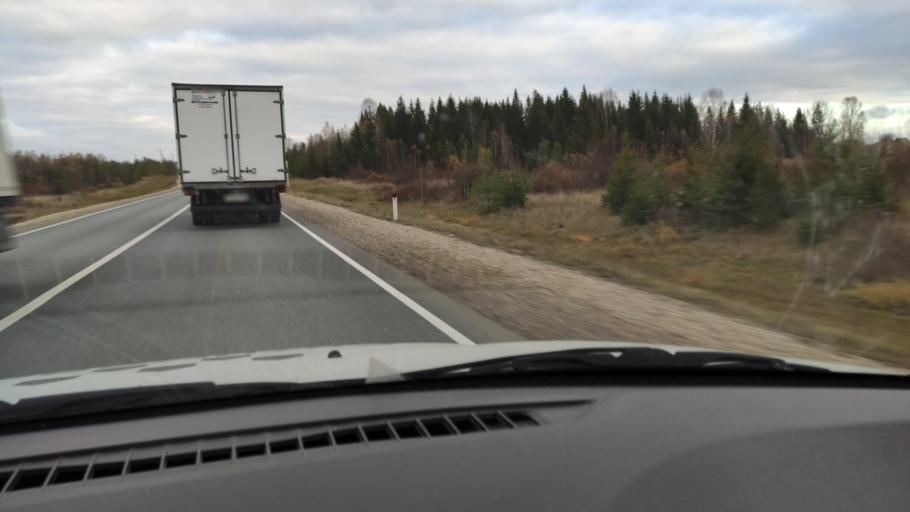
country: RU
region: Kirov
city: Chernaya Kholunitsa
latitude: 58.8589
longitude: 51.6982
